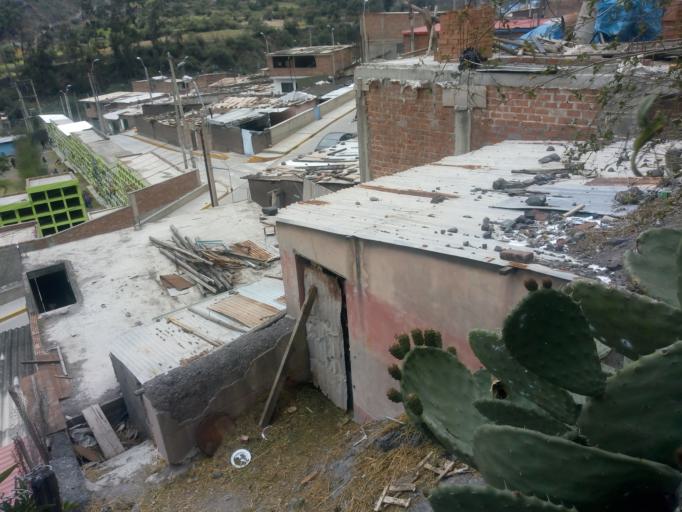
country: PE
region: Lima
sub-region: Provincia de Huarochiri
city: Matucana
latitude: -11.8424
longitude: -76.3793
